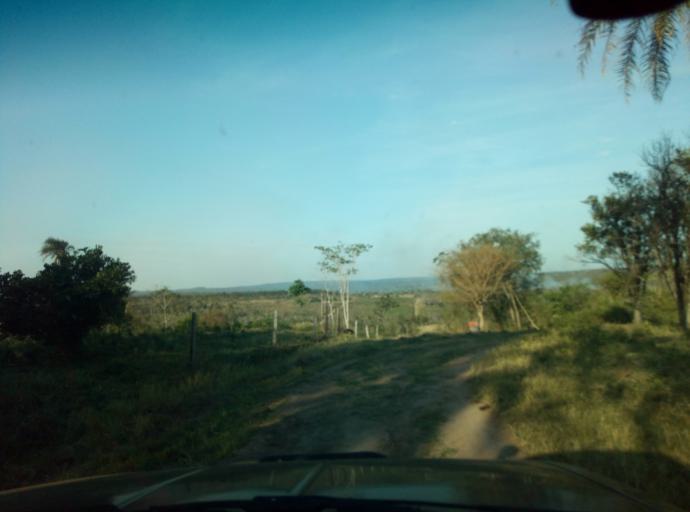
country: PY
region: Caaguazu
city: Doctor Cecilio Baez
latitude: -25.2000
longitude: -56.1306
